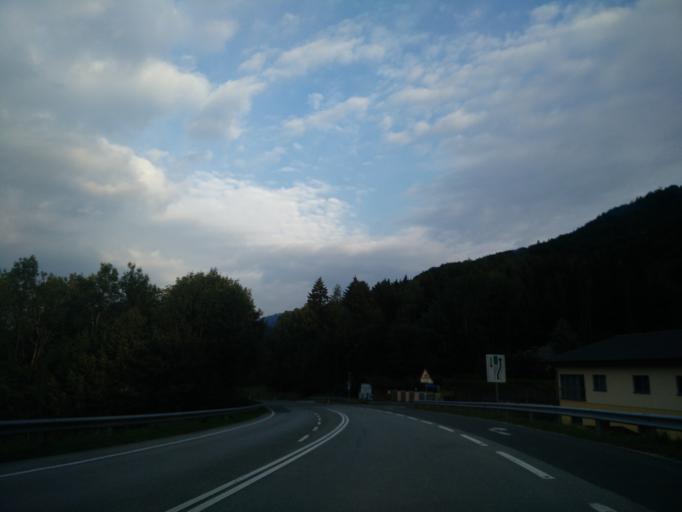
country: AT
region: Salzburg
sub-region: Politischer Bezirk Salzburg-Umgebung
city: Fuschl am See
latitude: 47.7936
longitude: 13.2832
